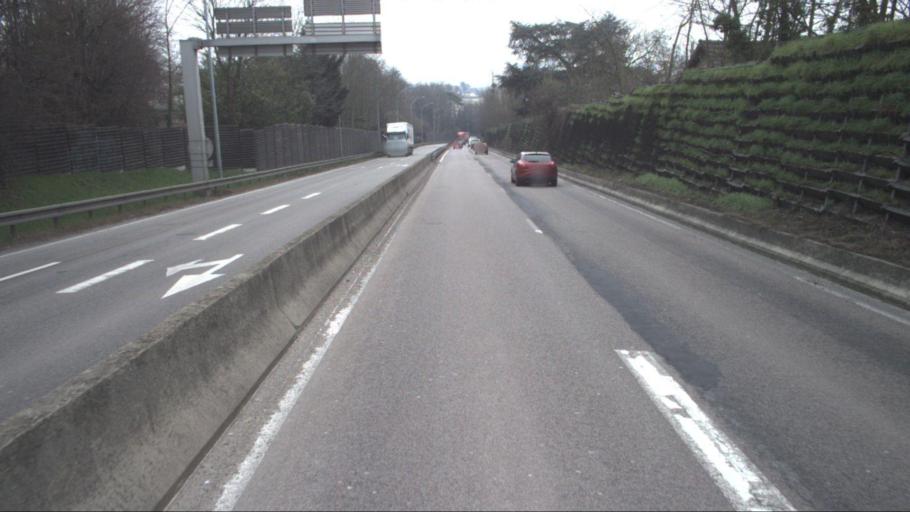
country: FR
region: Ile-de-France
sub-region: Departement des Yvelines
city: Saint-Germain-en-Laye
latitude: 48.8979
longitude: 2.0768
